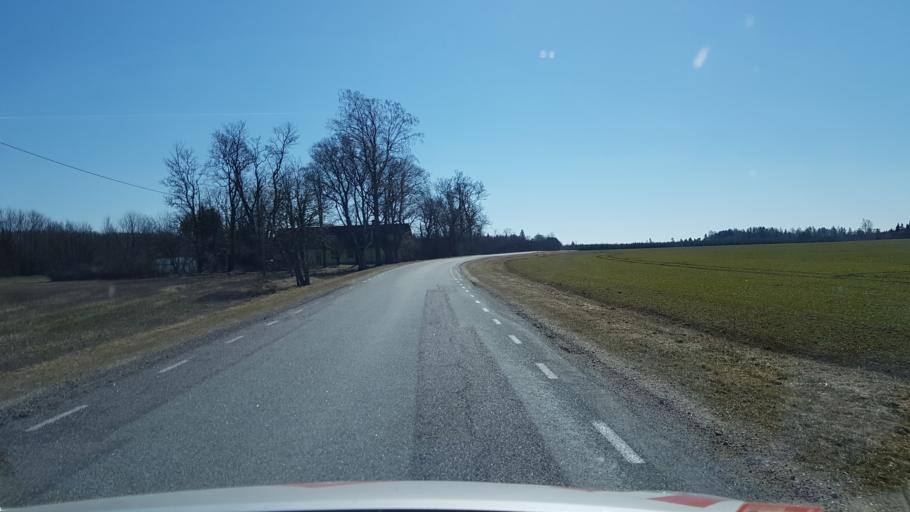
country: EE
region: Laeaene-Virumaa
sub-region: Rakke vald
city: Rakke
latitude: 59.0322
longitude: 26.3488
